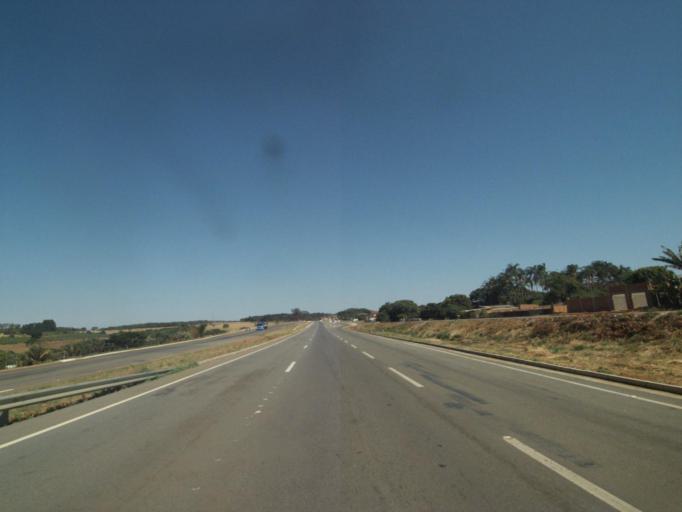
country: BR
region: Goias
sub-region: Anapolis
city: Anapolis
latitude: -16.1926
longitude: -49.0311
